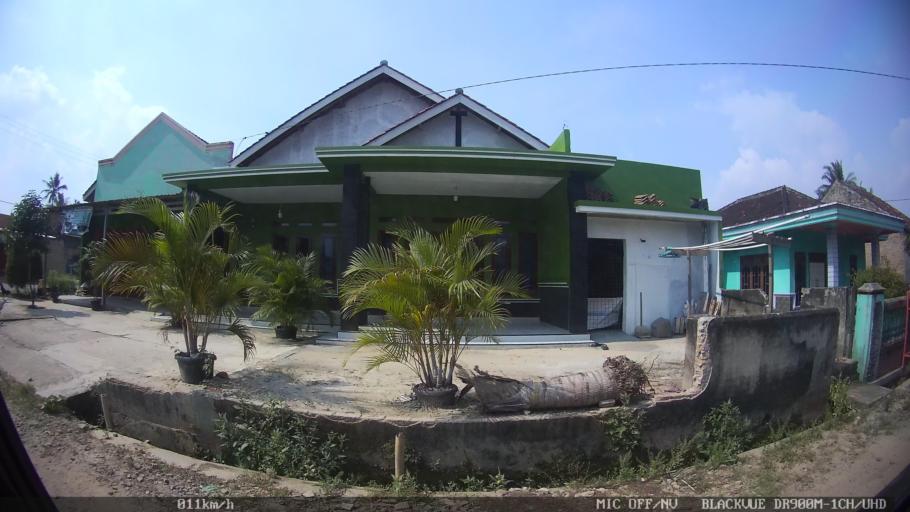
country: ID
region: Lampung
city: Natar
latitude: -5.2944
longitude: 105.2271
